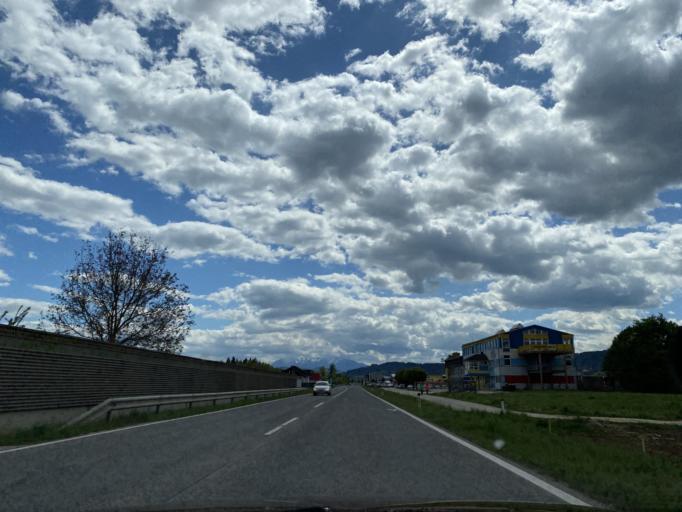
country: AT
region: Carinthia
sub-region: Politischer Bezirk Wolfsberg
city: Wolfsberg
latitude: 46.8069
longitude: 14.8307
